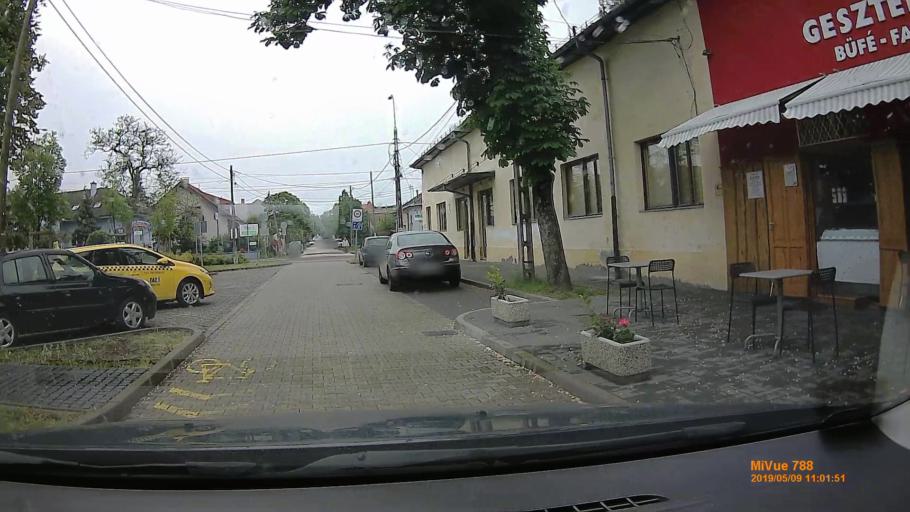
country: HU
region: Budapest
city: Budapest XVI. keruelet
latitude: 47.5231
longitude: 19.1626
